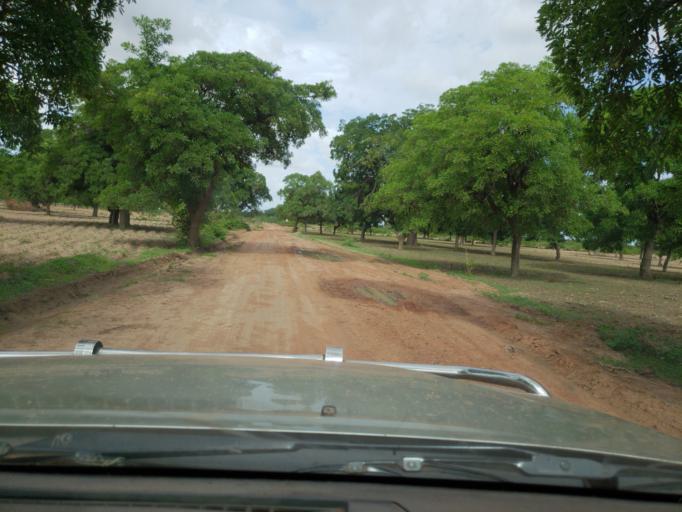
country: ML
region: Segou
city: Bla
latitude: 12.7081
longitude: -5.7080
